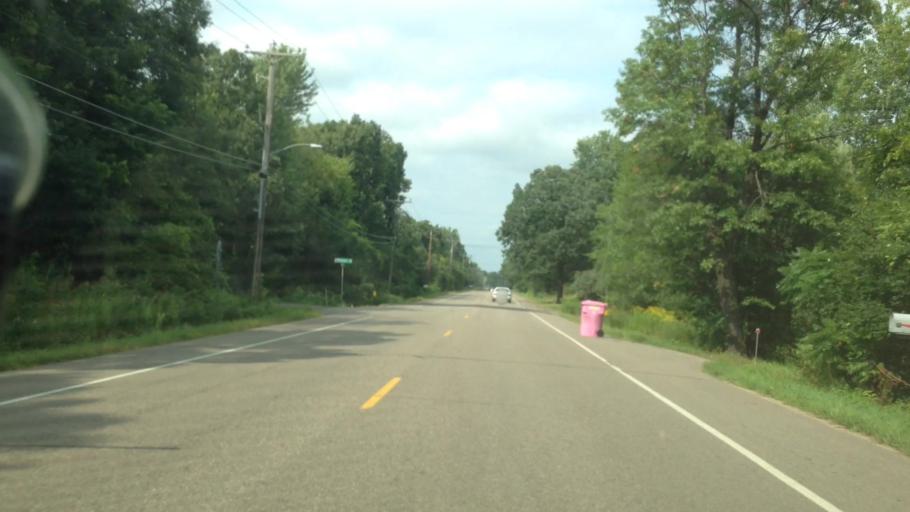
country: US
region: Minnesota
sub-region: Anoka County
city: Circle Pines
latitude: 45.1280
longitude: -93.1273
